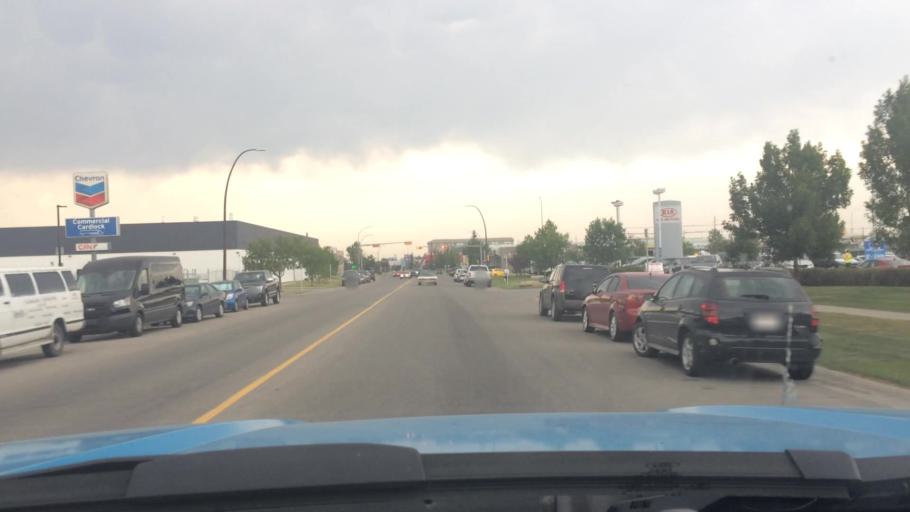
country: CA
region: Alberta
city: Calgary
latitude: 51.0719
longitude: -114.0041
